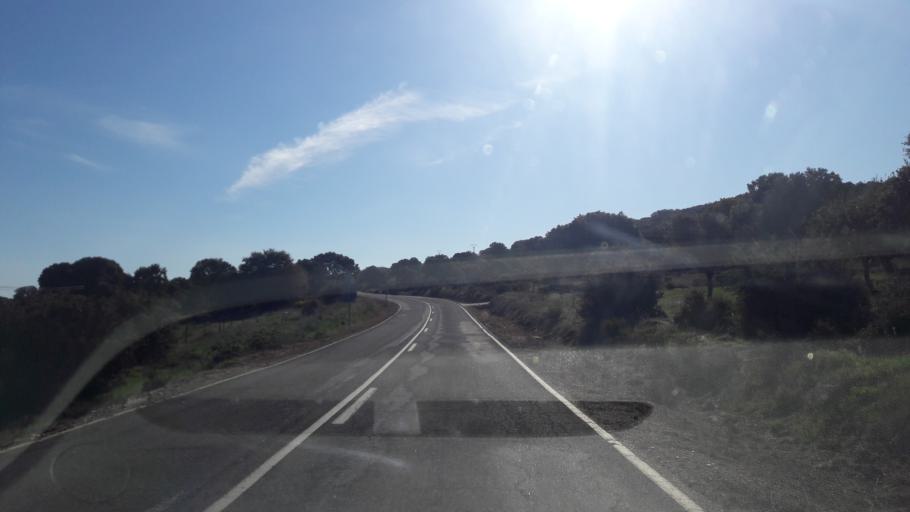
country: ES
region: Castille and Leon
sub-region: Provincia de Avila
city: Narrillos del Alamo
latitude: 40.5311
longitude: -5.4776
